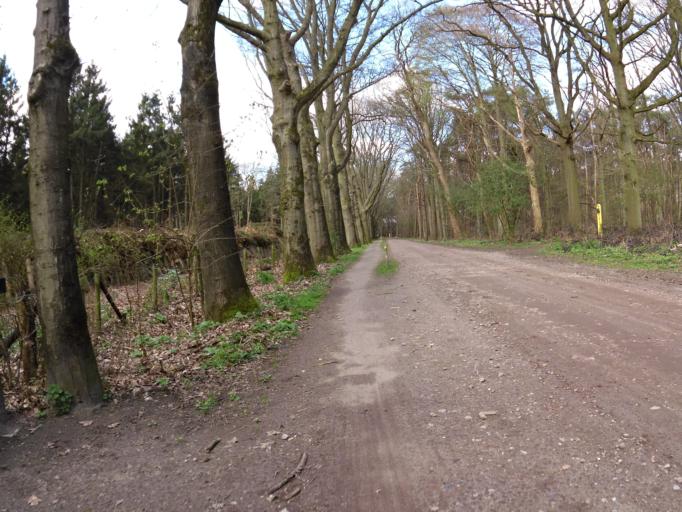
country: NL
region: North Brabant
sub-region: Gemeente Vught
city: Vught
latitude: 51.6370
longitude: 5.2666
